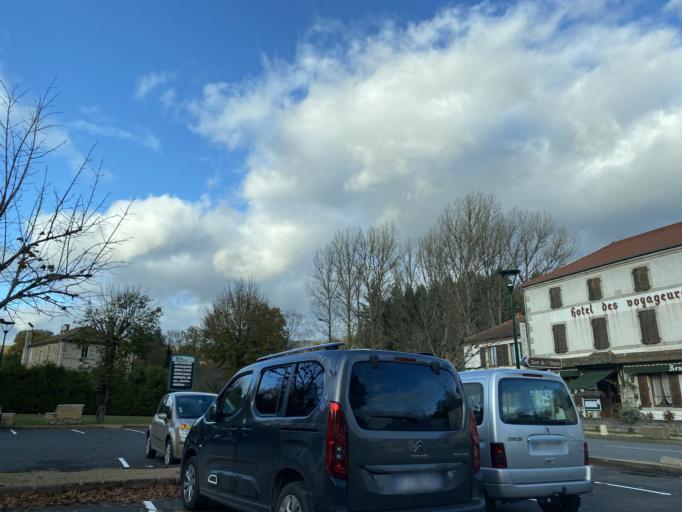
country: FR
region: Auvergne
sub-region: Departement du Puy-de-Dome
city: Job
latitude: 45.6429
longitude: 3.7059
